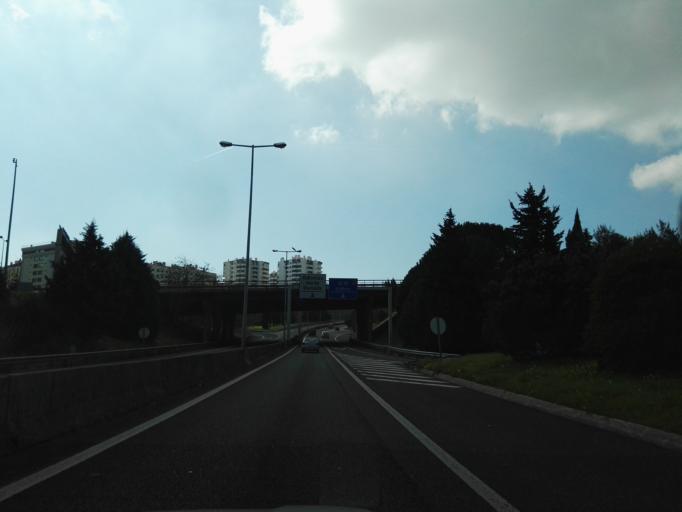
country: PT
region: Lisbon
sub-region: Odivelas
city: Povoa de Santo Adriao
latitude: 38.8027
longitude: -9.1773
